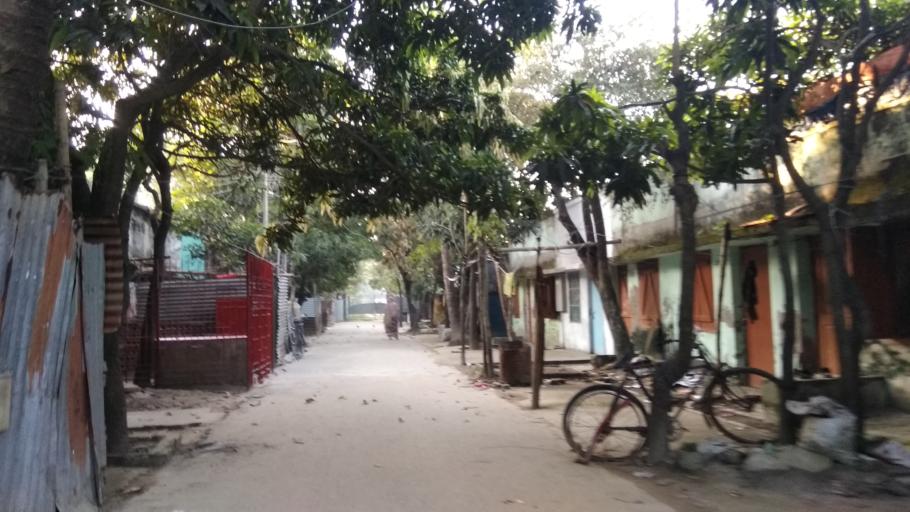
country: BD
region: Dhaka
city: Tungi
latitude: 23.8437
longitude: 90.4213
